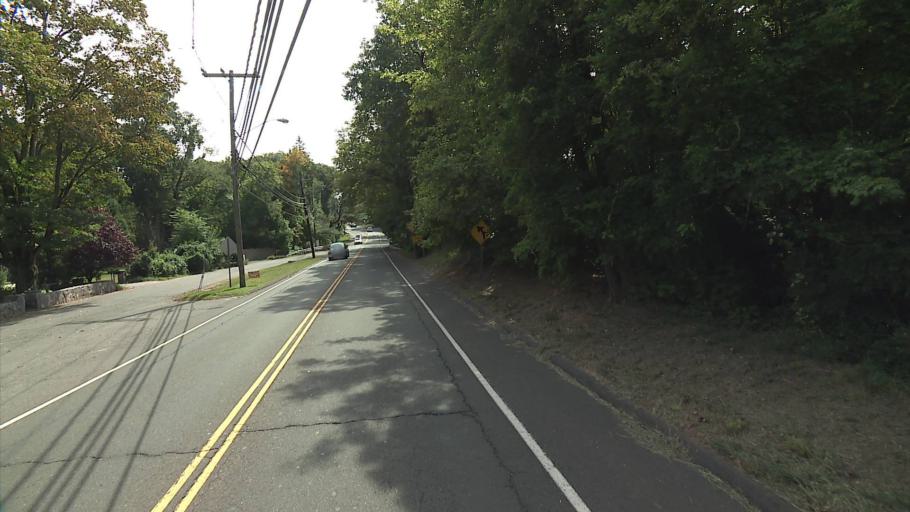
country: US
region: Connecticut
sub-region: Fairfield County
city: North Stamford
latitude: 41.1246
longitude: -73.5445
